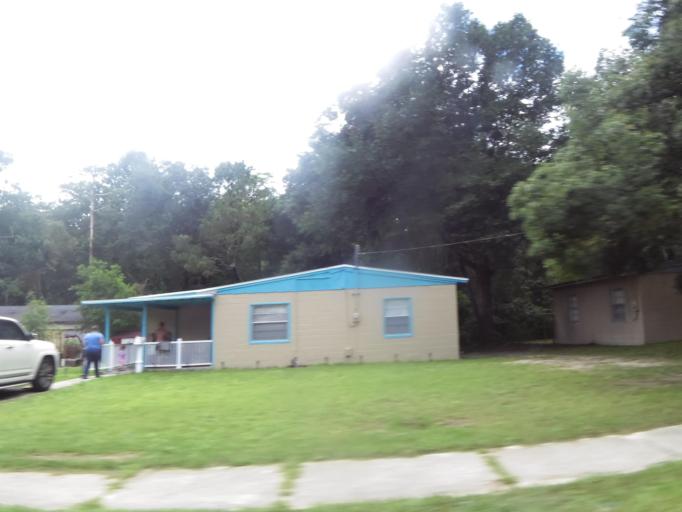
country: US
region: Florida
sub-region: Duval County
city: Jacksonville
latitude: 30.2788
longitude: -81.5551
